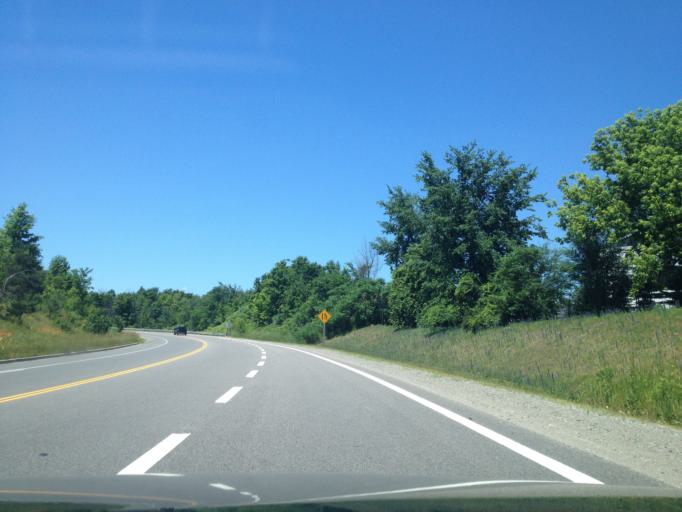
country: CA
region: Ontario
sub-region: Halton
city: Milton
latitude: 43.6735
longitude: -79.9843
